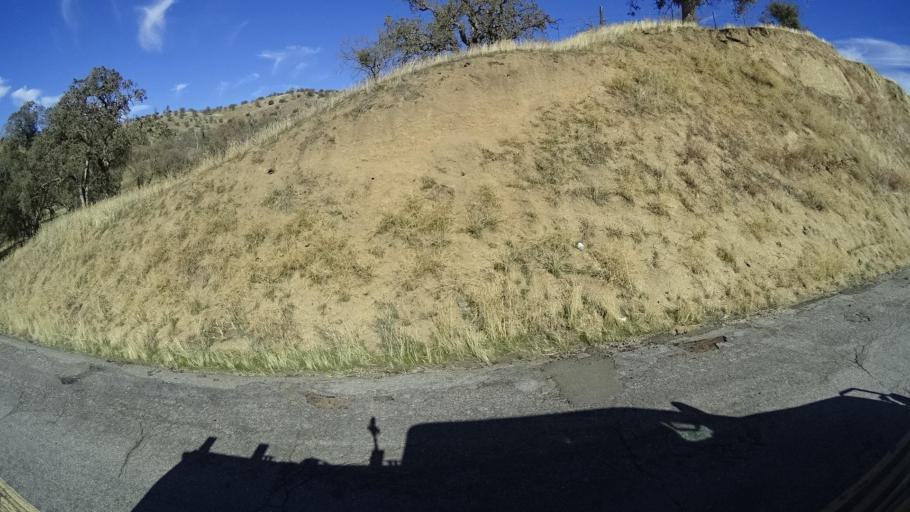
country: US
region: California
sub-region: Kern County
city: Alta Sierra
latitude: 35.6297
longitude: -118.7884
